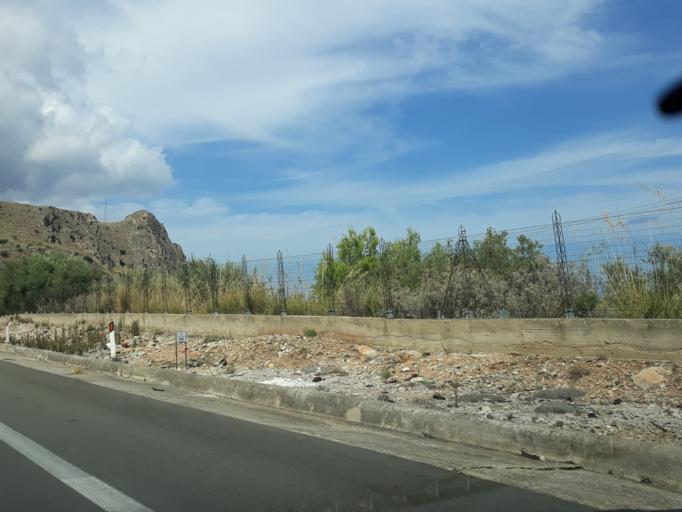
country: IT
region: Sicily
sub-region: Palermo
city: Trabia
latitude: 37.9830
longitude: 13.6620
